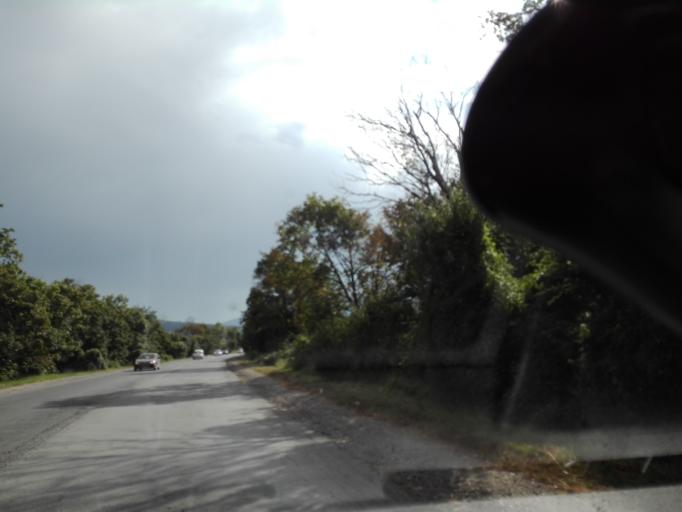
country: BG
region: Sofia-Capital
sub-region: Stolichna Obshtina
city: Sofia
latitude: 42.6248
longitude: 23.4442
